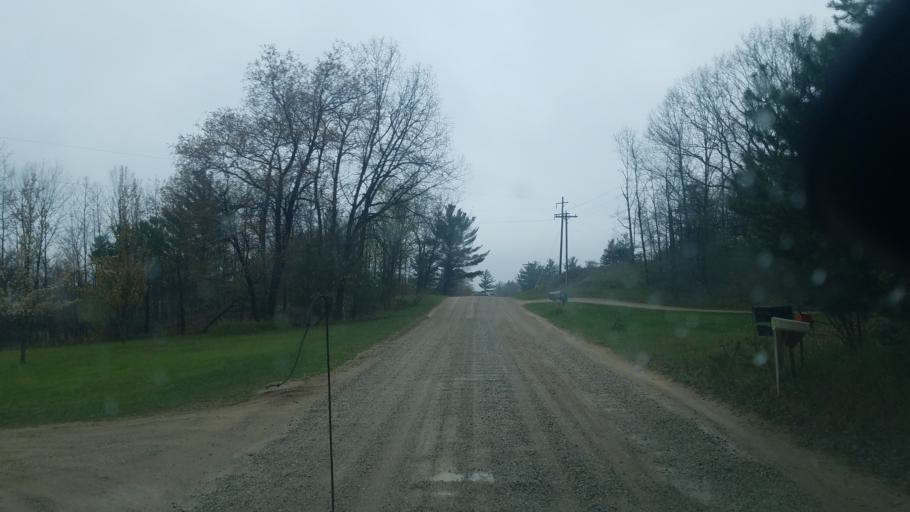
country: US
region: Michigan
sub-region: Montcalm County
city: Lakeview
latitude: 43.4702
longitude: -85.2937
